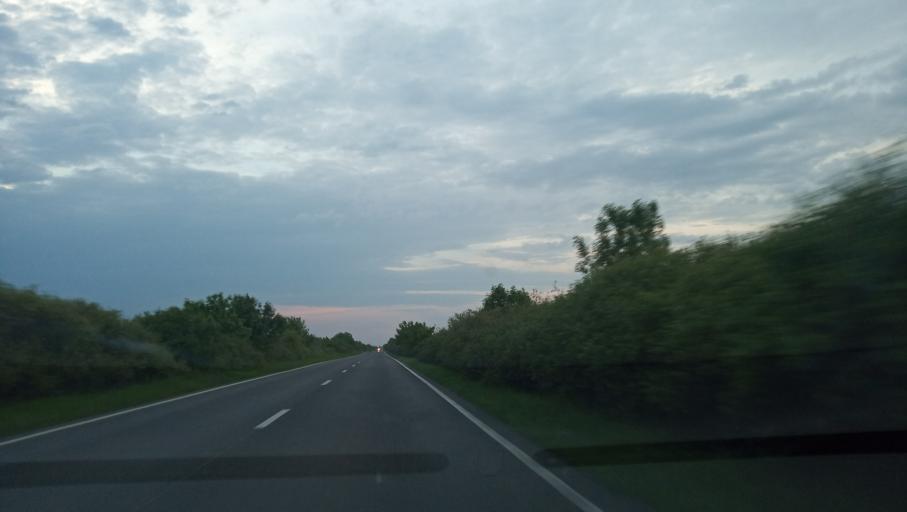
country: RO
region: Timis
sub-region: Comuna Jebel
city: Jebel
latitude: 45.5316
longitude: 21.2295
